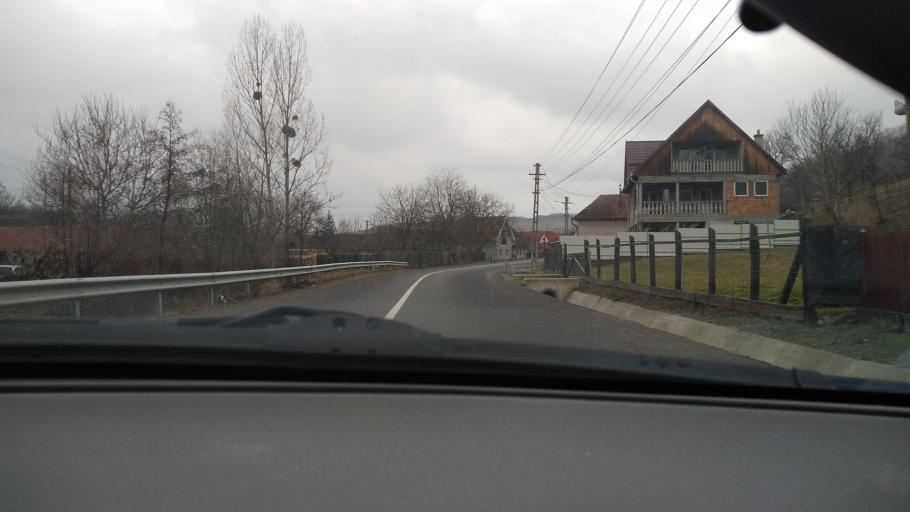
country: RO
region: Mures
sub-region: Comuna Magherani
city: Magherani
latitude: 46.5633
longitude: 24.9140
